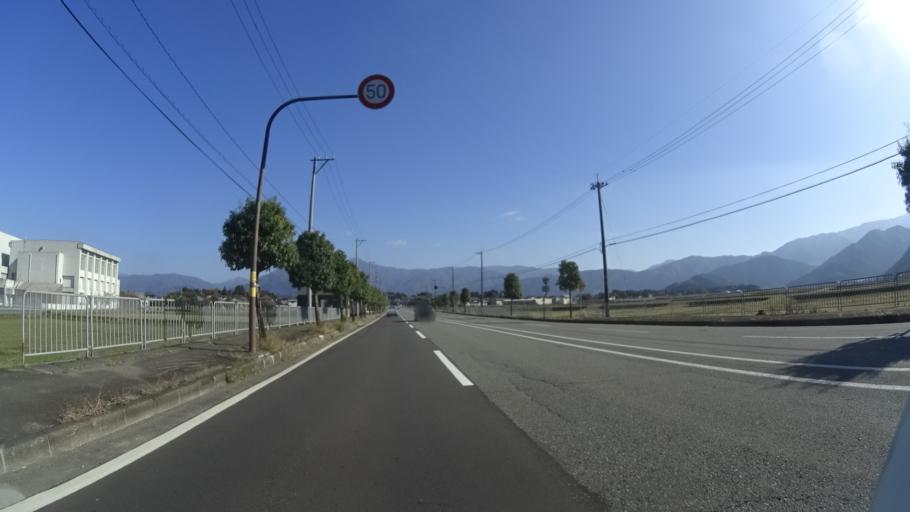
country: JP
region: Fukui
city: Ono
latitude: 35.9722
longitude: 136.4826
